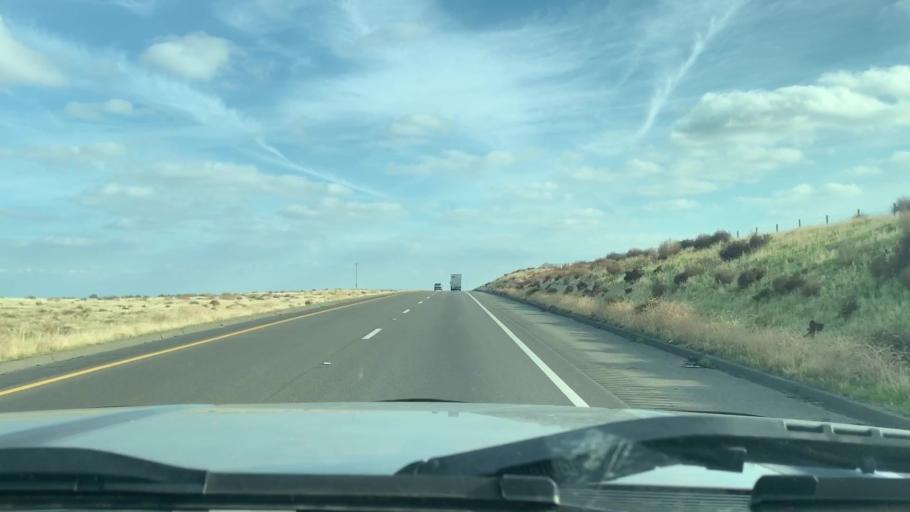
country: US
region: California
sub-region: Kings County
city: Kettleman City
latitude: 36.0224
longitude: -120.0104
